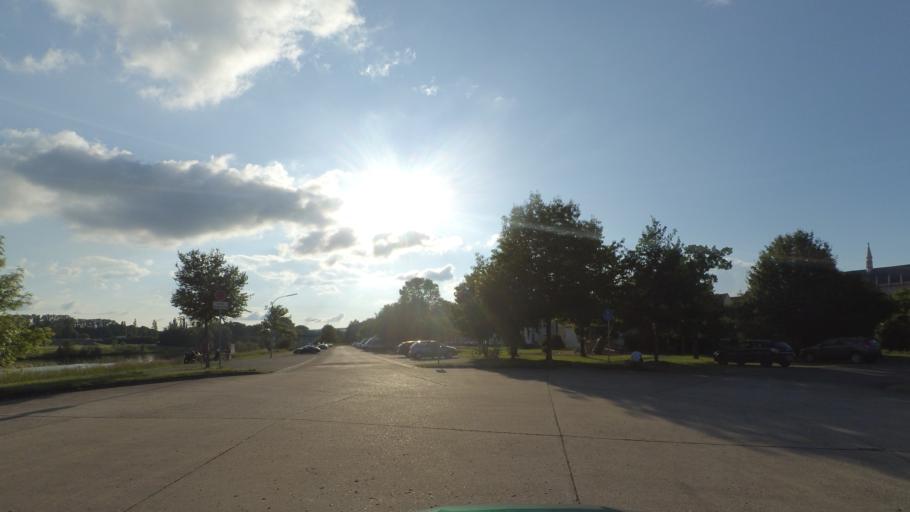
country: DE
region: Bavaria
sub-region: Regierungsbezirk Unterfranken
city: Hassfurt
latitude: 50.0297
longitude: 10.5130
